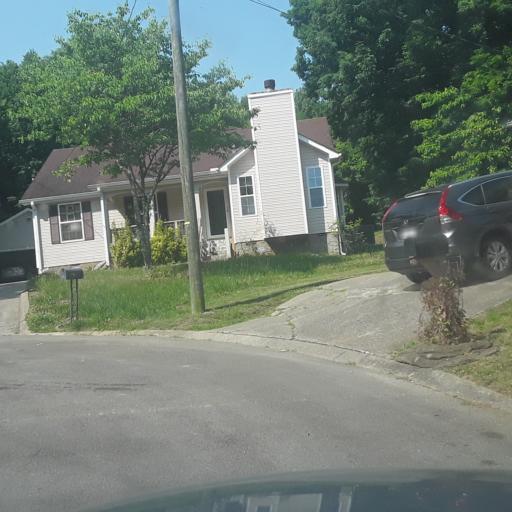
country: US
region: Tennessee
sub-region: Williamson County
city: Brentwood Estates
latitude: 36.0389
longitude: -86.7102
